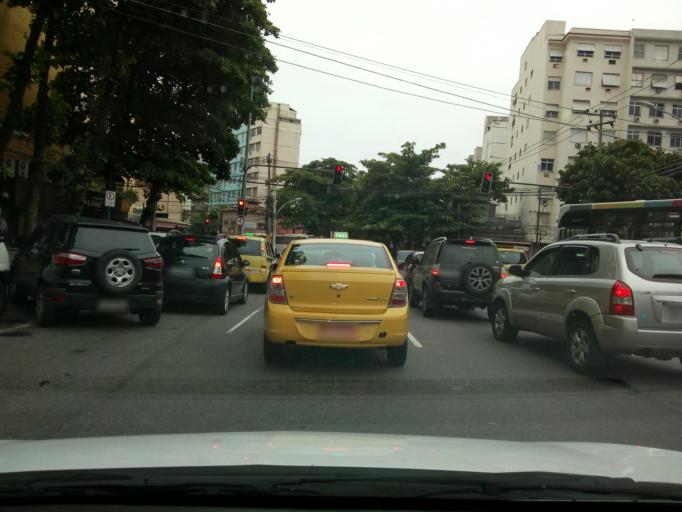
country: BR
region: Rio de Janeiro
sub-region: Rio De Janeiro
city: Rio de Janeiro
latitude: -22.9228
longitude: -43.2335
